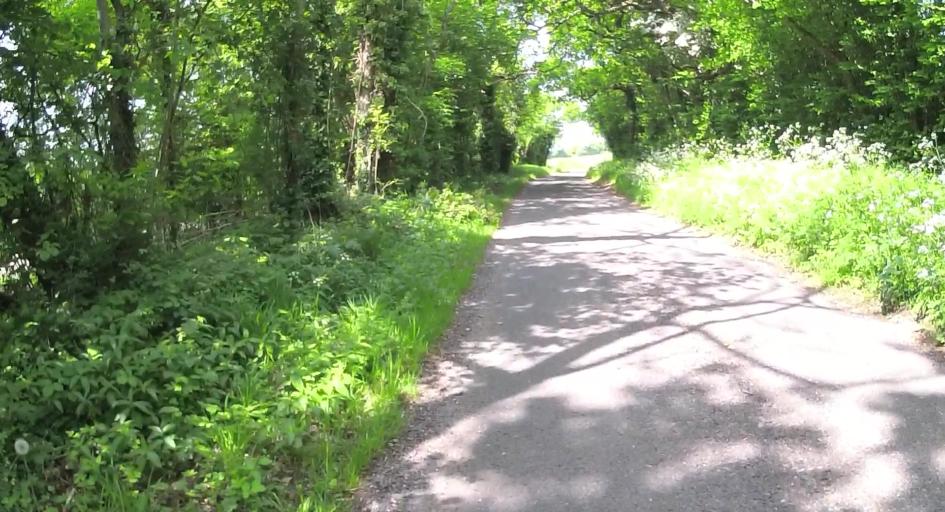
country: GB
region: England
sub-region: Hampshire
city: Overton
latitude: 51.2703
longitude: -1.2331
